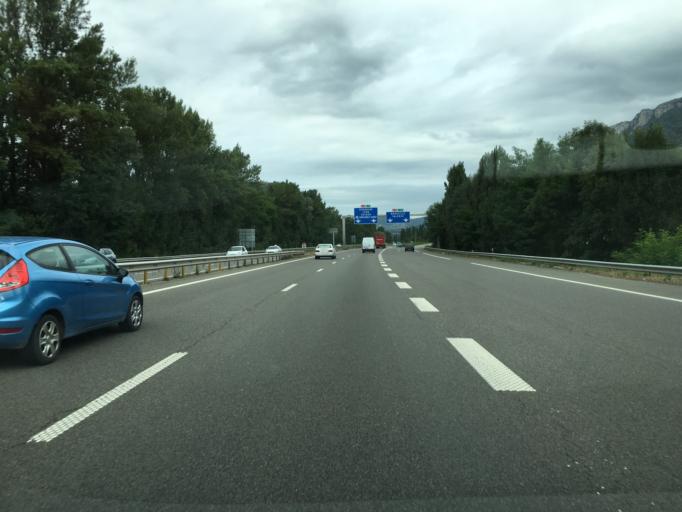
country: FR
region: Rhone-Alpes
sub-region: Departement de l'Isere
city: Voreppe
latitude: 45.2898
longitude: 5.6202
